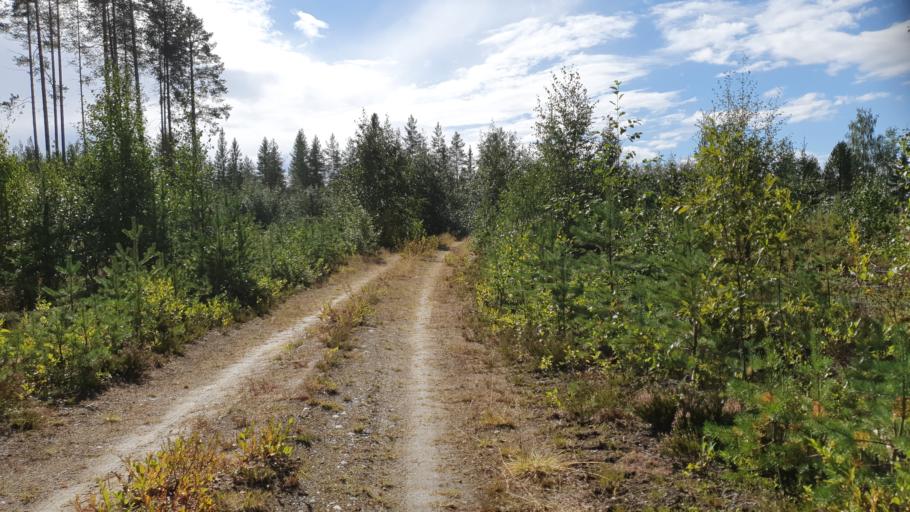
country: FI
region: Kainuu
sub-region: Kehys-Kainuu
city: Kuhmo
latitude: 64.1304
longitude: 29.3796
